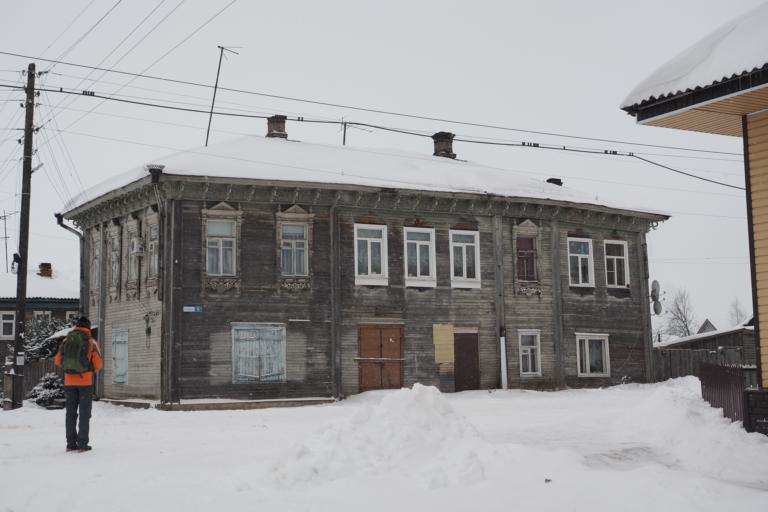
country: RU
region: Tverskaya
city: Ves'yegonsk
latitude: 58.6796
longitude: 37.2572
